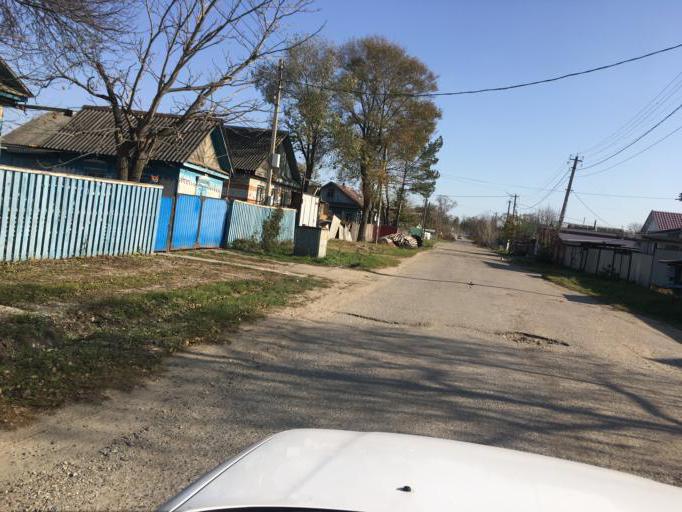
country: RU
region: Primorskiy
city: Dal'nerechensk
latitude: 45.9252
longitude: 133.7230
